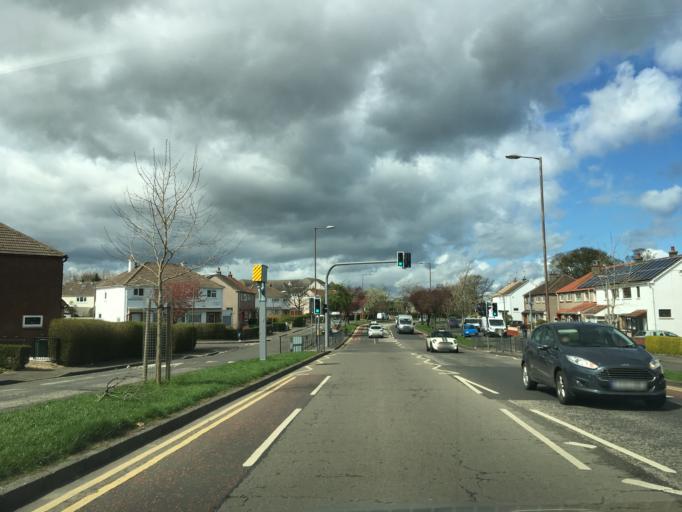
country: GB
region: Scotland
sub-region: Edinburgh
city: Currie
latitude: 55.9377
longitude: -3.2919
